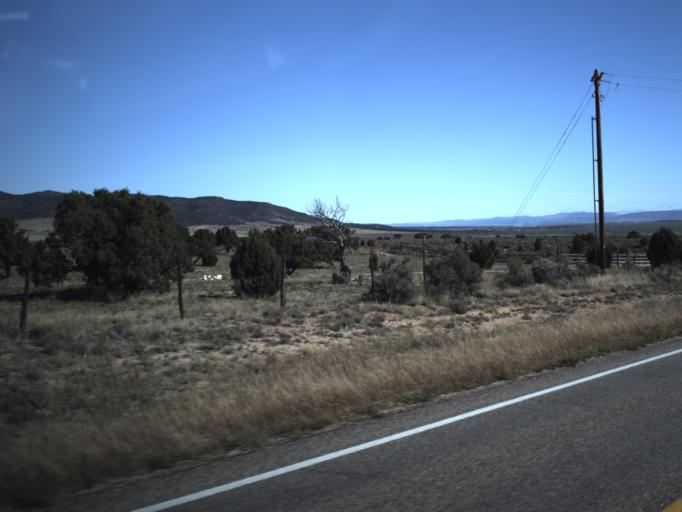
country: US
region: Utah
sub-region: Iron County
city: Cedar City
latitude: 37.6451
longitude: -113.2449
